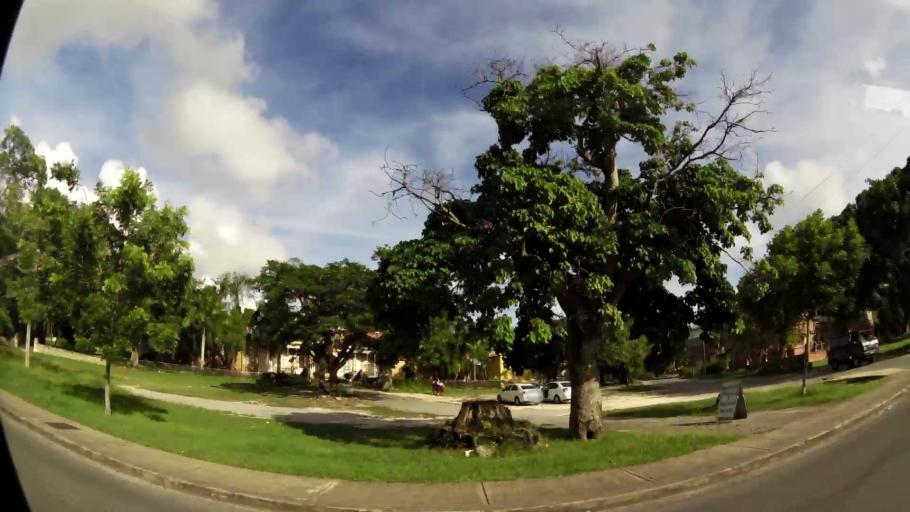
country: BB
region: Saint Michael
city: Bridgetown
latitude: 13.0832
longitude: -59.6030
